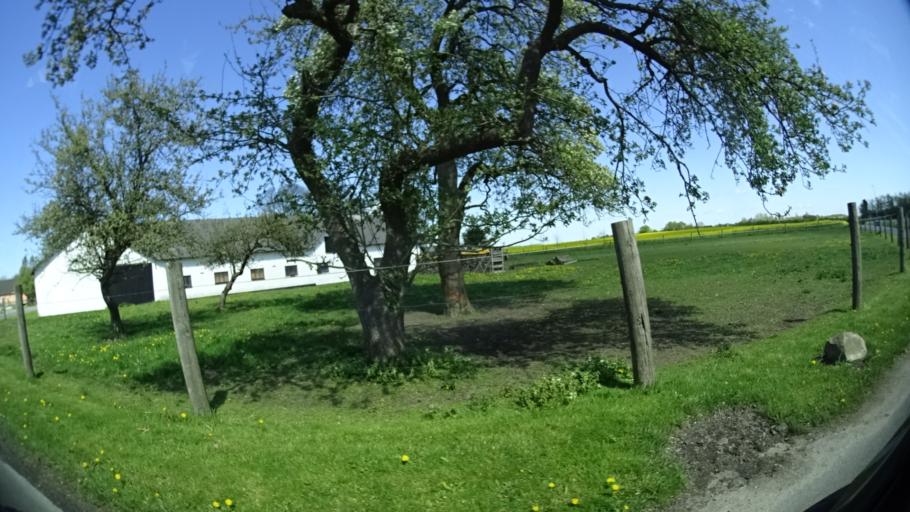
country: DK
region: Central Jutland
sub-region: Randers Kommune
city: Assentoft
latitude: 56.4147
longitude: 10.0937
